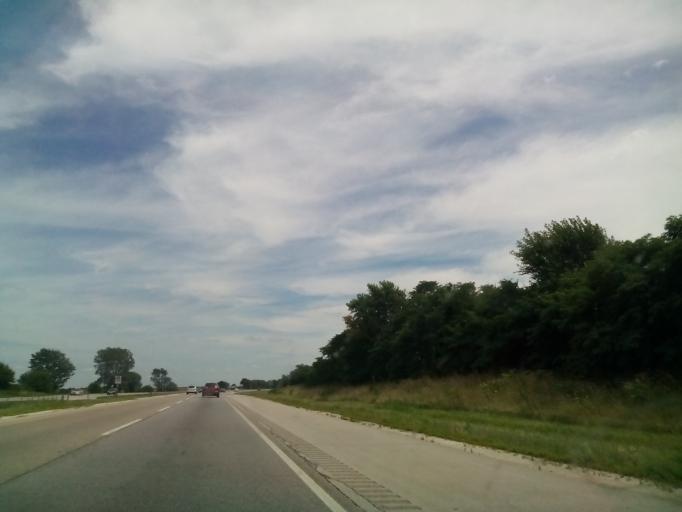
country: US
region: Illinois
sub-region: DeKalb County
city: Cortland
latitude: 41.9009
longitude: -88.6556
